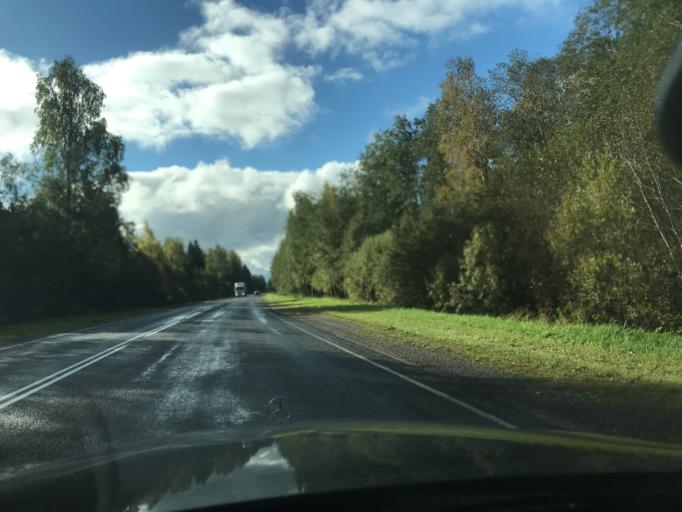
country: EE
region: Tartu
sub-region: Elva linn
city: Elva
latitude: 57.9987
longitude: 26.2679
